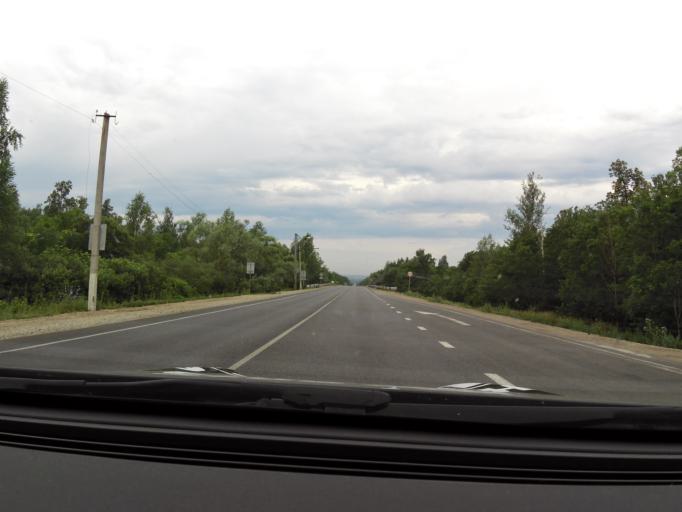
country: RU
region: Bashkortostan
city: Ulu-Telyak
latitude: 54.8415
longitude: 57.0572
